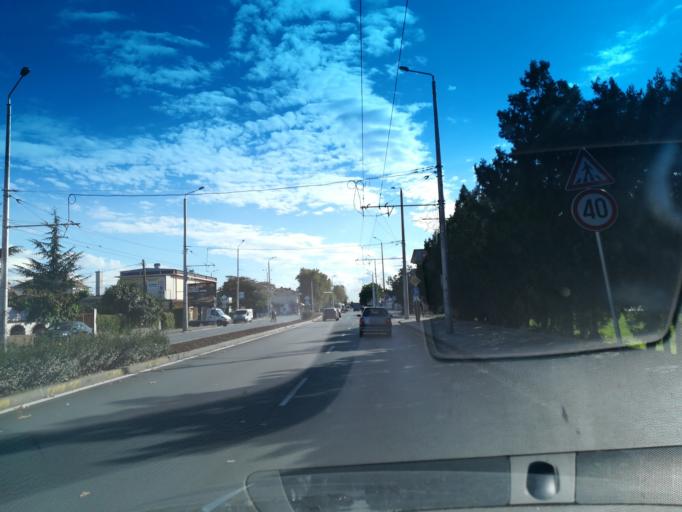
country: BG
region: Stara Zagora
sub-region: Obshtina Stara Zagora
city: Stara Zagora
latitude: 42.3999
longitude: 25.6439
